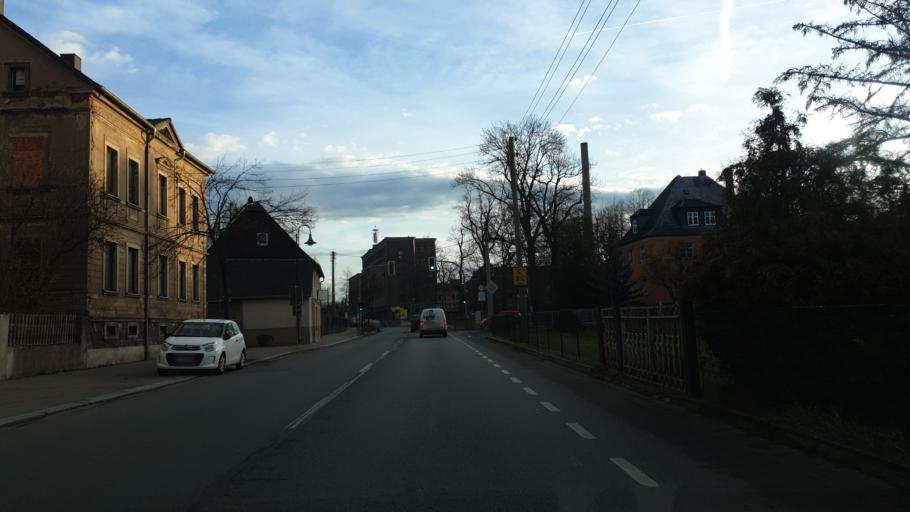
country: DE
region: Saxony
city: Oberlungwitz
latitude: 50.7847
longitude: 12.7170
